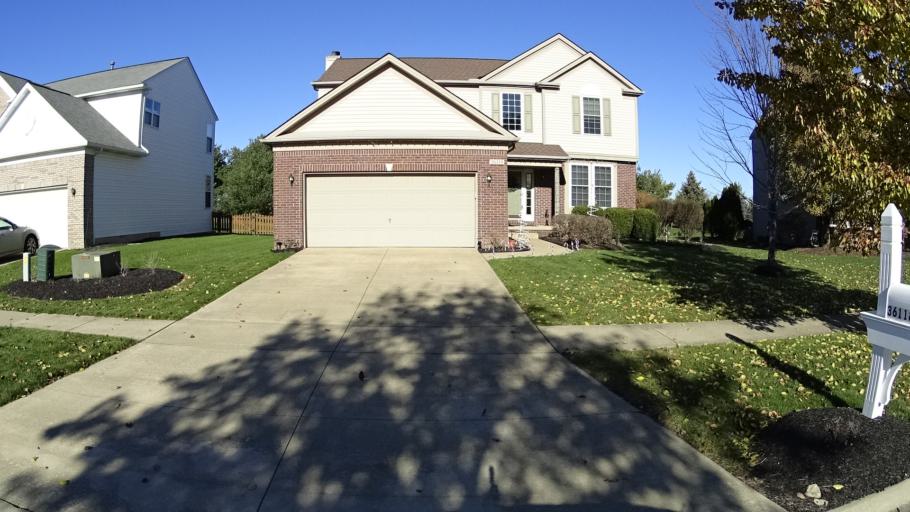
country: US
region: Ohio
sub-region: Lorain County
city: Avon
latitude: 41.4337
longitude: -82.0236
